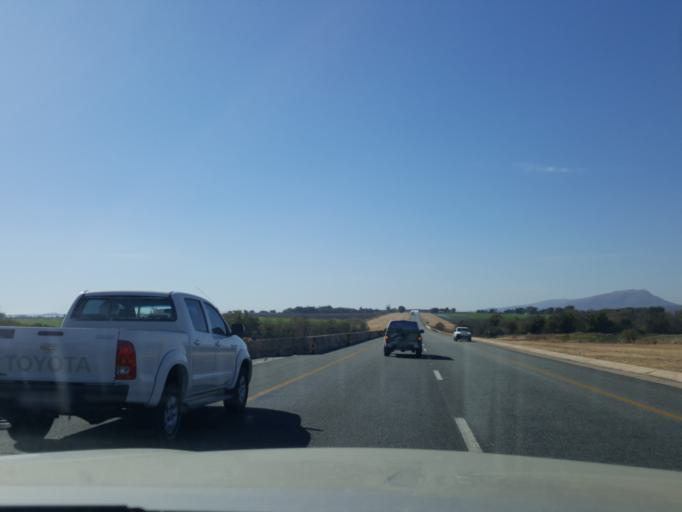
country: ZA
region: North-West
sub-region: Bojanala Platinum District Municipality
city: Brits
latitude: -25.6816
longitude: 27.8004
